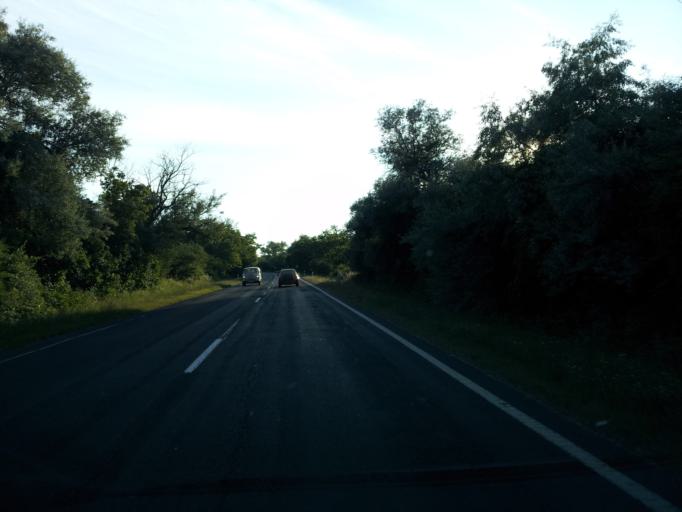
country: HU
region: Fejer
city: Szarliget
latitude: 47.4855
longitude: 18.5634
